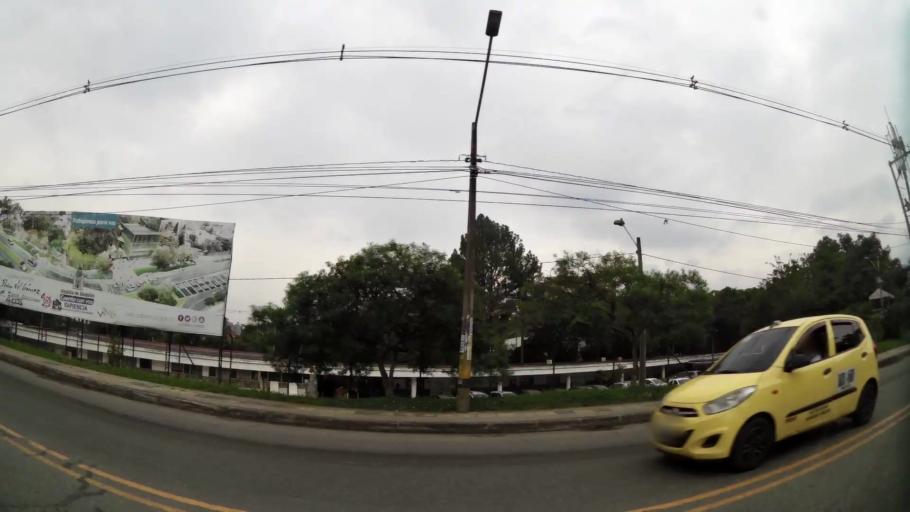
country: CO
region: Antioquia
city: Medellin
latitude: 6.2731
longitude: -75.5875
